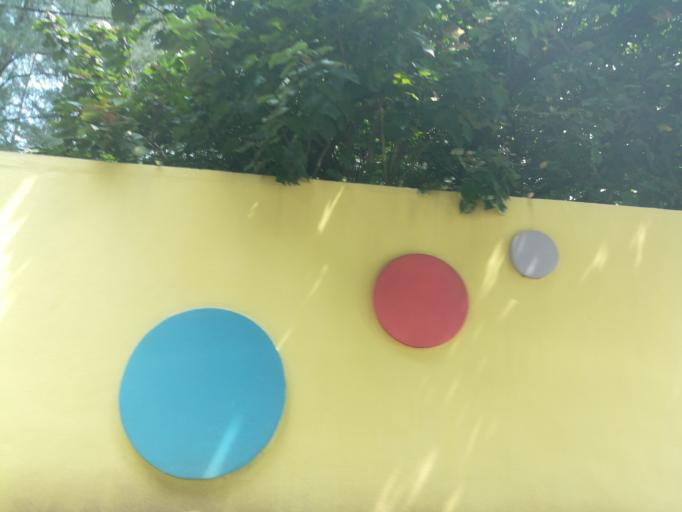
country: NG
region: Lagos
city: Ikeja
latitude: 6.6059
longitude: 3.3631
